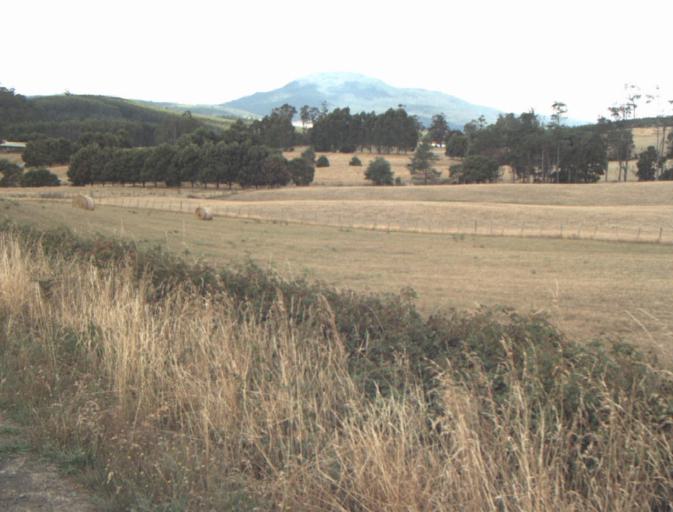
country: AU
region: Tasmania
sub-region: Launceston
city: Mayfield
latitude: -41.1983
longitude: 147.2216
